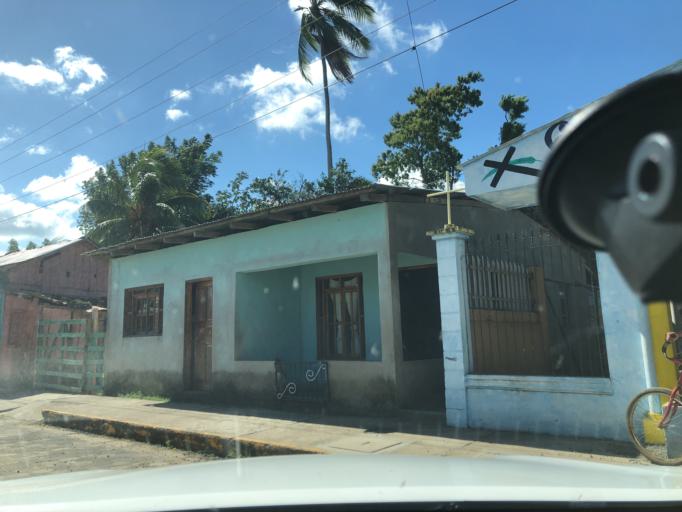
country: NI
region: Rivas
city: Cardenas
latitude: 11.1964
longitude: -85.5098
